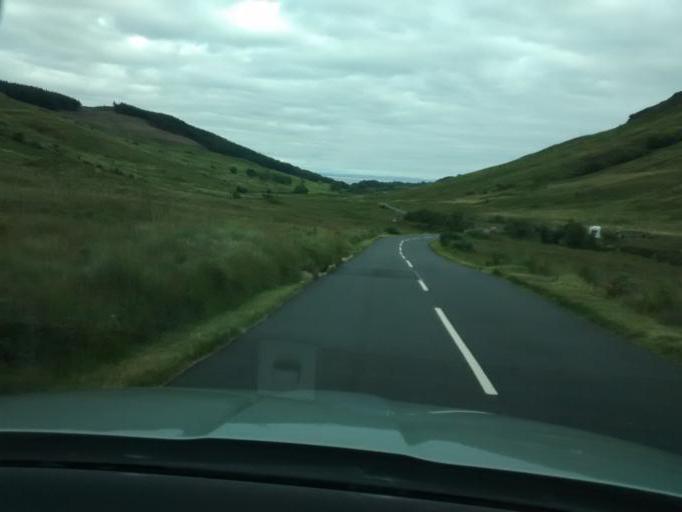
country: GB
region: Scotland
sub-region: North Ayrshire
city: Isle of Arran
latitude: 55.6738
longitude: -5.1954
